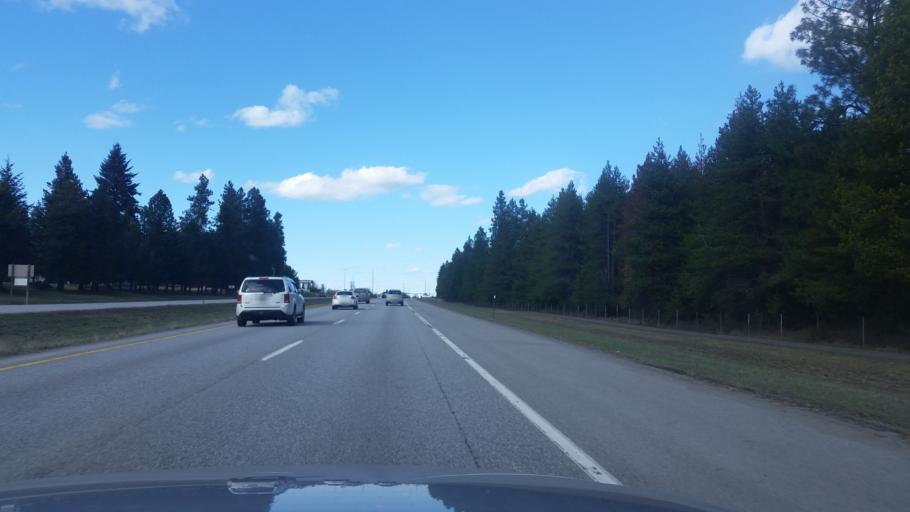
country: US
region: Idaho
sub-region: Kootenai County
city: Dalton Gardens
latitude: 47.7378
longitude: -116.7926
